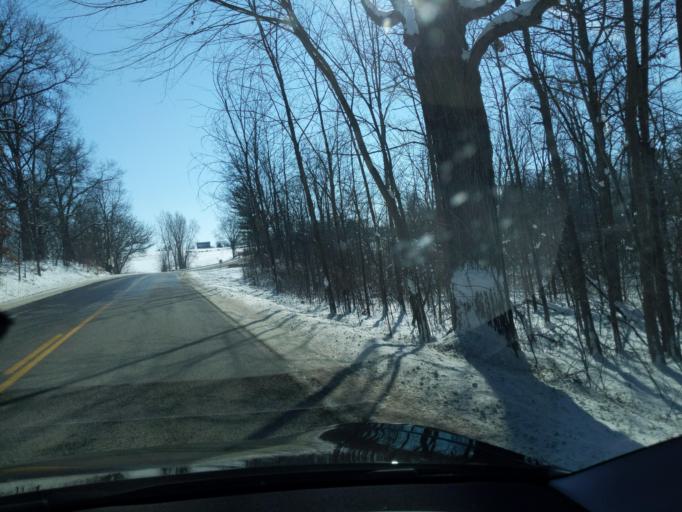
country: US
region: Michigan
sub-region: Livingston County
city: Fowlerville
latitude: 42.5699
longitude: -84.0716
